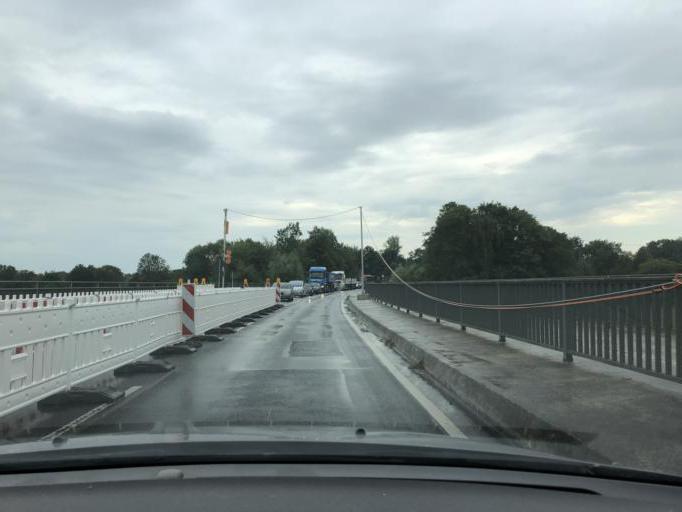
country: DE
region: North Rhine-Westphalia
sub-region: Regierungsbezirk Dusseldorf
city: Schermbeck
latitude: 51.6743
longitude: 6.8606
